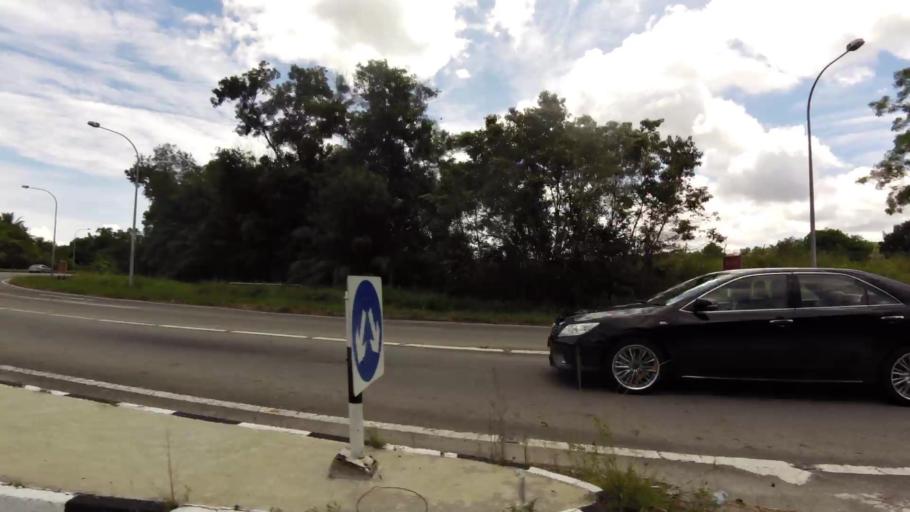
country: BN
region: Brunei and Muara
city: Bandar Seri Begawan
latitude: 4.9547
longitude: 114.9173
